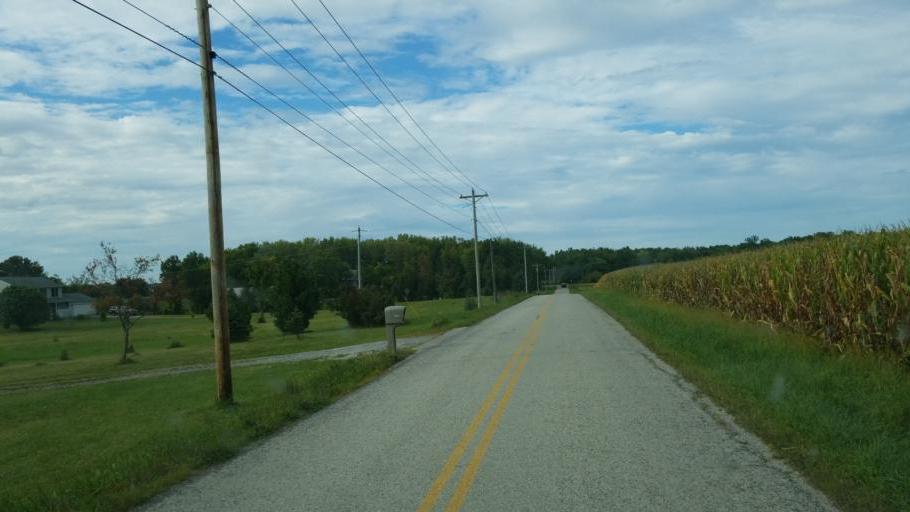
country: US
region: Ohio
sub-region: Knox County
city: Centerburg
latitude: 40.3168
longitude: -82.7714
